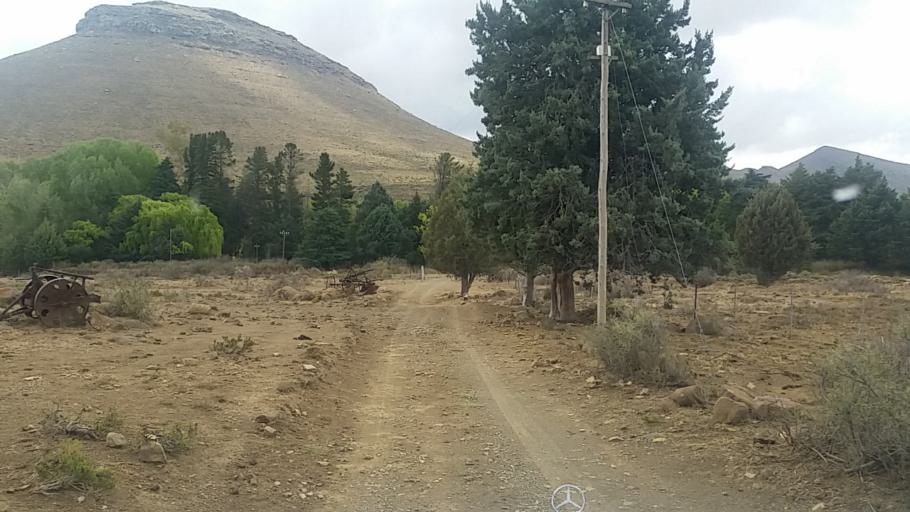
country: ZA
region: Eastern Cape
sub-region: Chris Hani District Municipality
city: Middelburg
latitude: -31.7905
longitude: 24.6620
